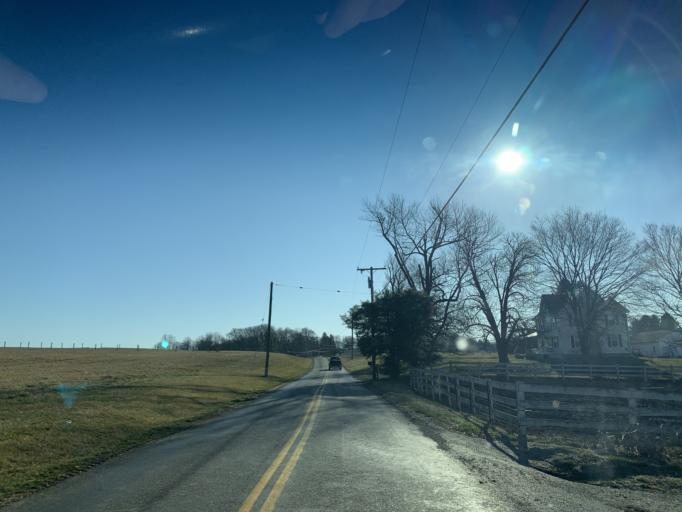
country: US
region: Maryland
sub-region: Harford County
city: Aberdeen
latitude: 39.5858
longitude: -76.2093
